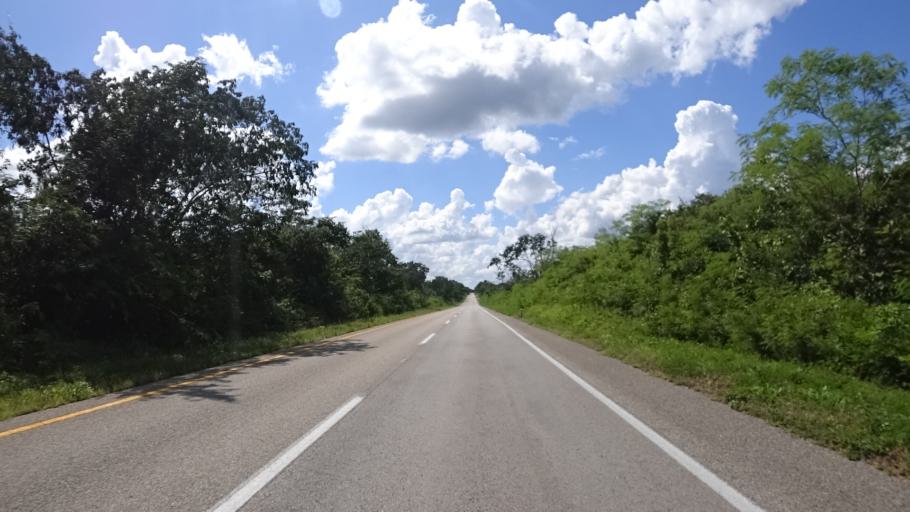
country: MX
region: Yucatan
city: Chichen-Itza
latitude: 20.7154
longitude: -88.5073
